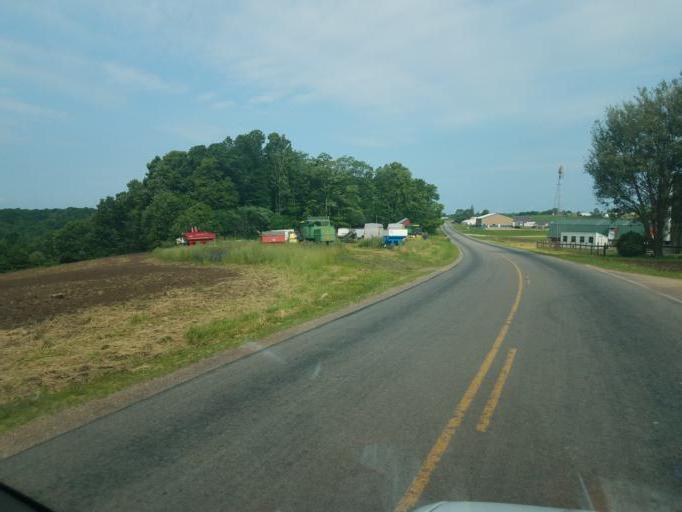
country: US
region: Wisconsin
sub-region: Vernon County
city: Hillsboro
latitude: 43.6113
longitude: -90.4390
